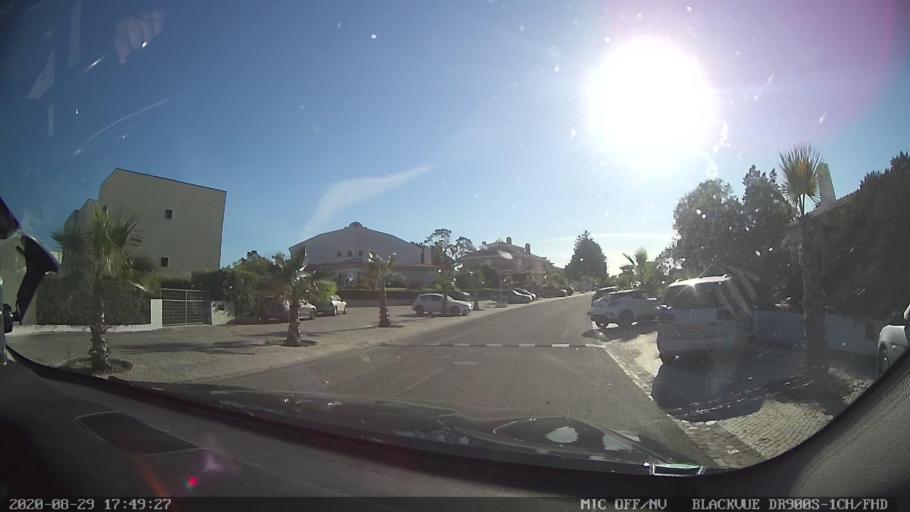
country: PT
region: Setubal
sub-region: Setubal
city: Setubal
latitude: 38.4536
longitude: -8.8584
